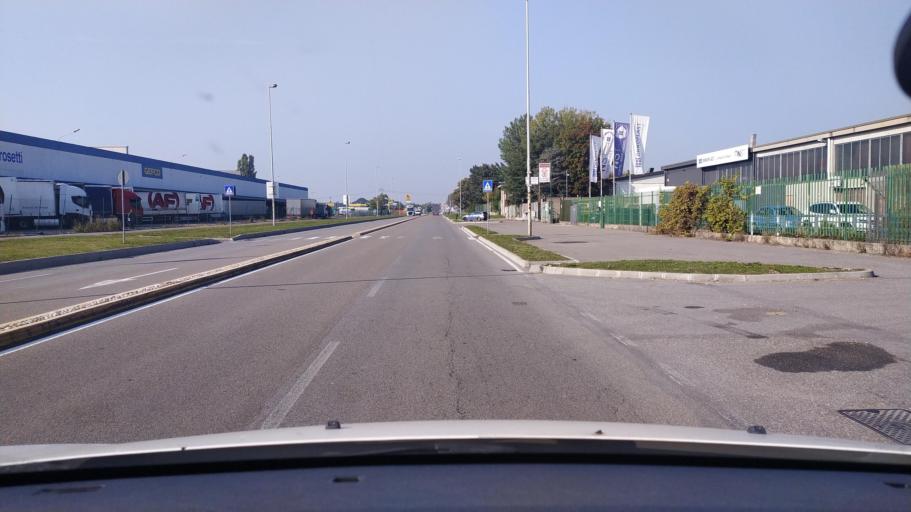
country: IT
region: Lombardy
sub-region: Citta metropolitana di Milano
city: Cusago
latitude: 45.4375
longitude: 9.0461
